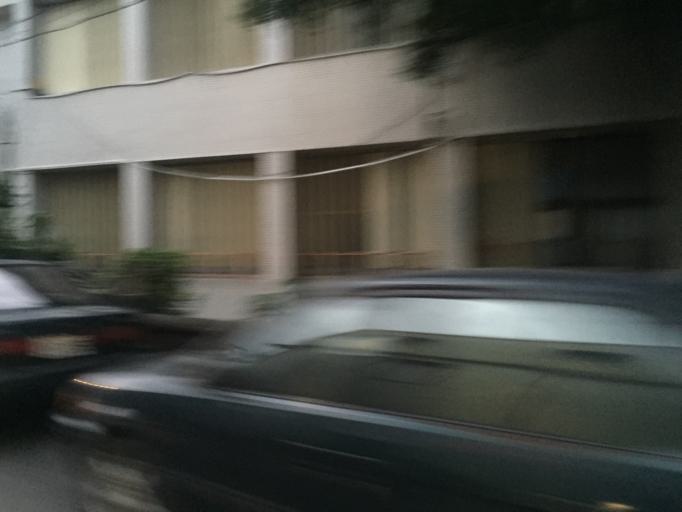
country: TW
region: Taiwan
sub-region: Yilan
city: Yilan
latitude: 24.7553
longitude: 121.7460
